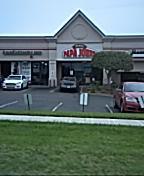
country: US
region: Kentucky
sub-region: Jefferson County
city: Hurstbourne
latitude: 38.2419
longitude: -85.5768
